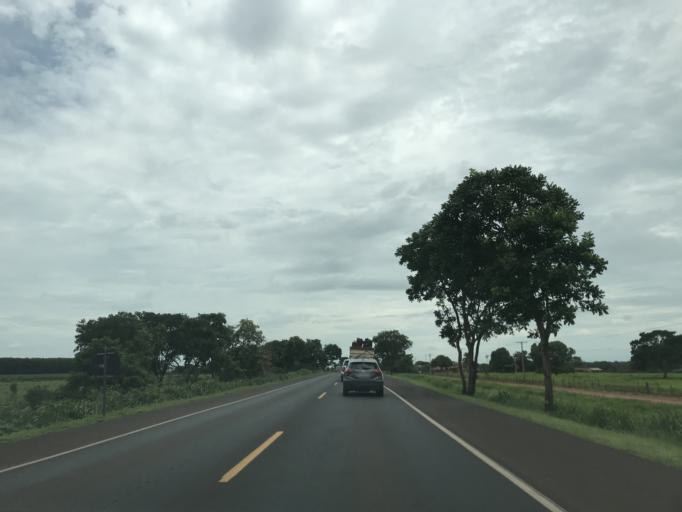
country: BR
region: Sao Paulo
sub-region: Nova Granada
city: Nova Granada
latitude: -20.2672
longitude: -49.1831
